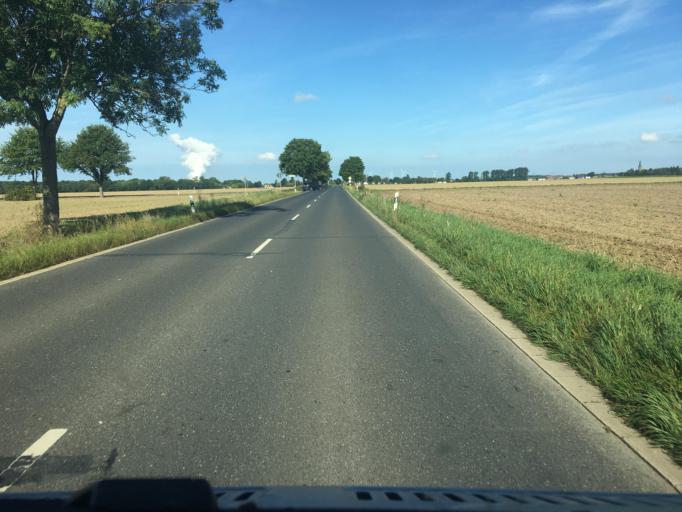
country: DE
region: North Rhine-Westphalia
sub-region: Regierungsbezirk Koln
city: Dueren
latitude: 50.7786
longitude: 6.4516
